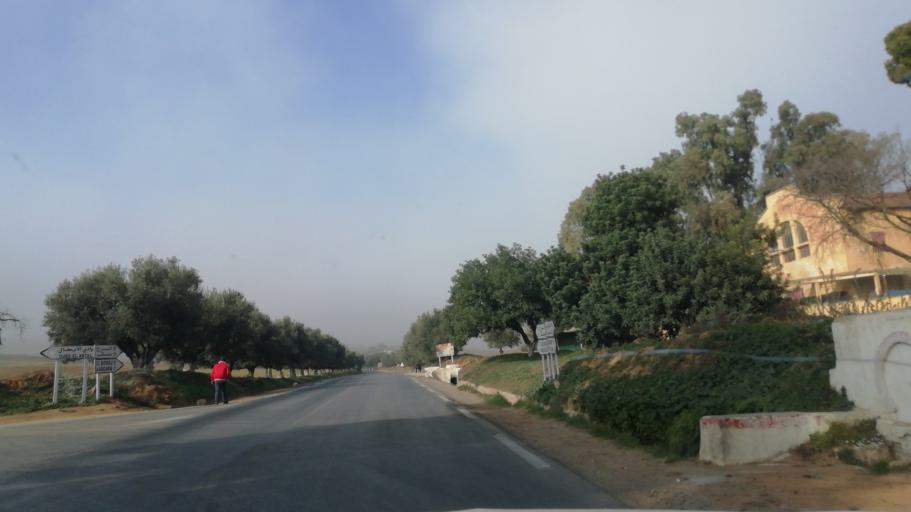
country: DZ
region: Mascara
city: Mascara
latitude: 35.5355
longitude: 0.3591
